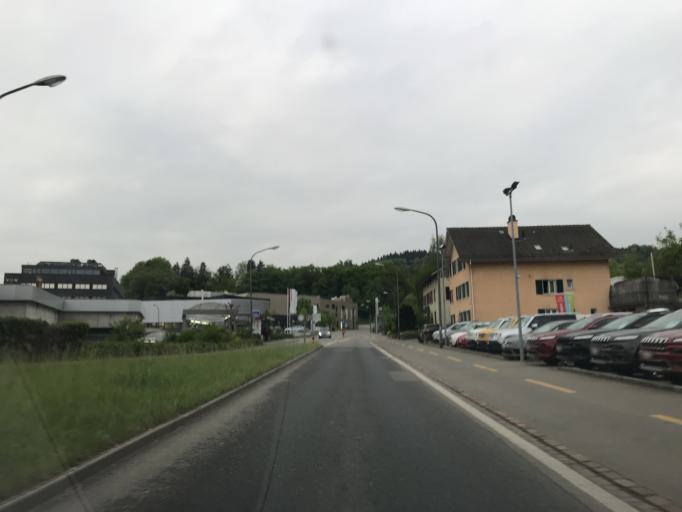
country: CH
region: Zurich
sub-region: Bezirk Winterthur
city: Toss
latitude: 47.4783
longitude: 8.7036
